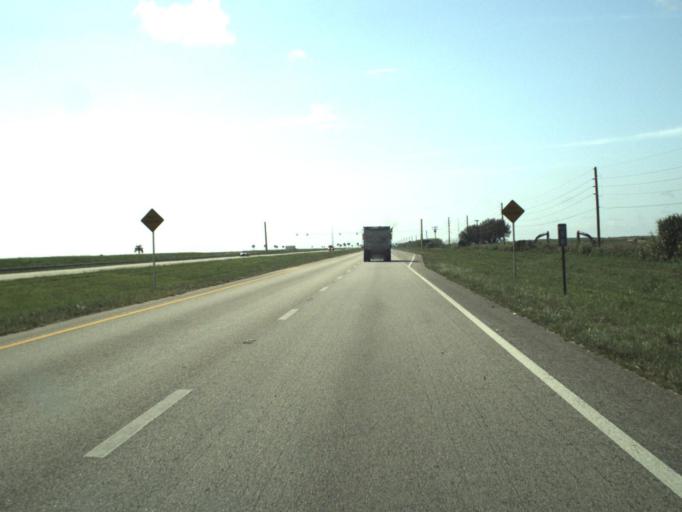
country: US
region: Florida
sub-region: Palm Beach County
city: Belle Glade Camp
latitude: 26.4614
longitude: -80.6359
